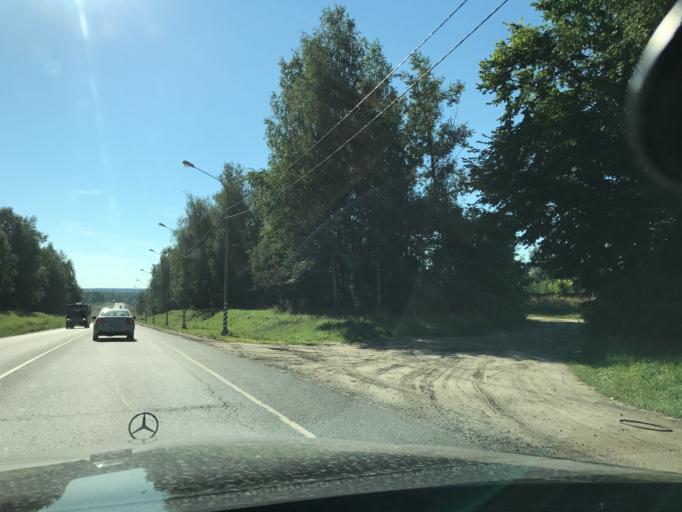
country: RU
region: Moskovskaya
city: Noginsk-9
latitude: 56.1079
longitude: 38.6246
